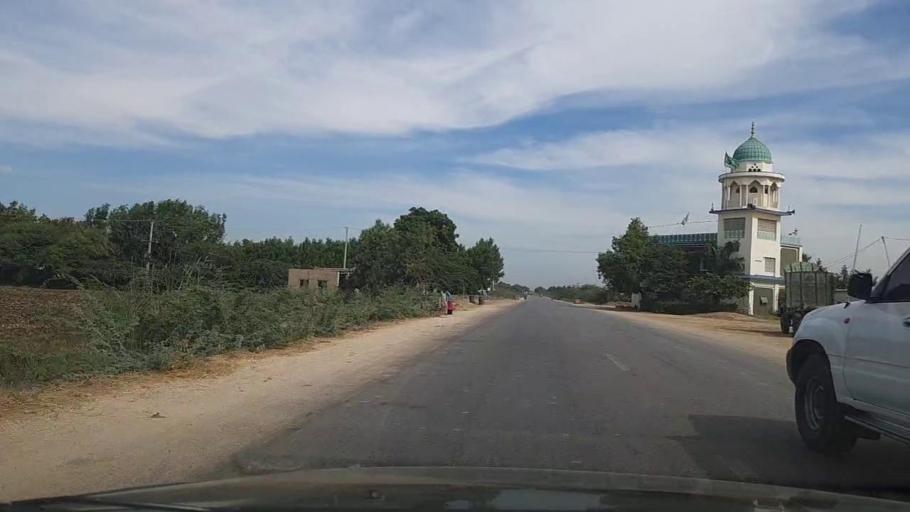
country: PK
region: Sindh
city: Thatta
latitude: 24.7845
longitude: 67.9512
